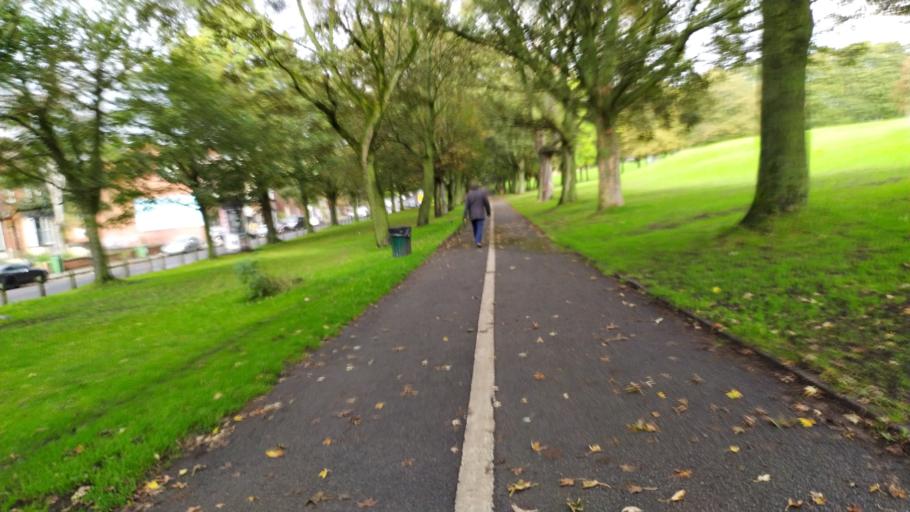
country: GB
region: England
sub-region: City and Borough of Leeds
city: Leeds
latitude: 53.8113
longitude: -1.5644
